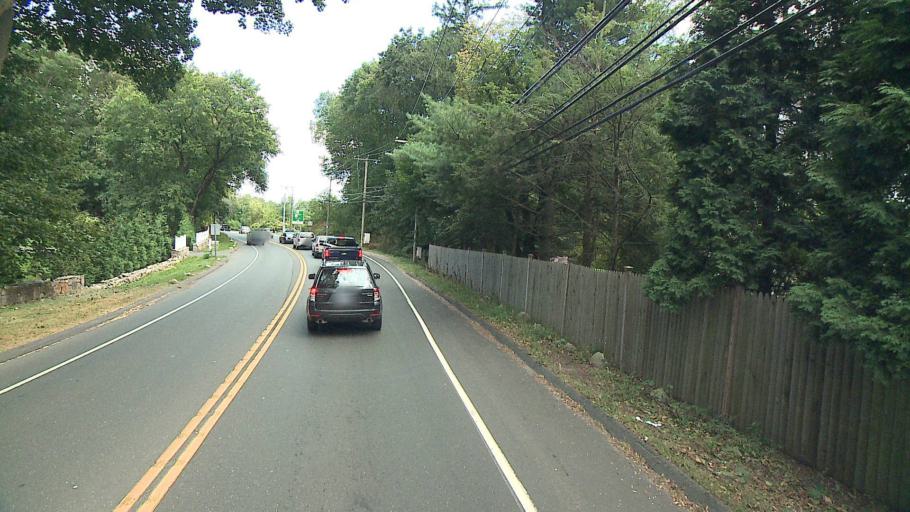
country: US
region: Connecticut
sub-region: Fairfield County
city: Westport
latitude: 41.1652
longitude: -73.3793
